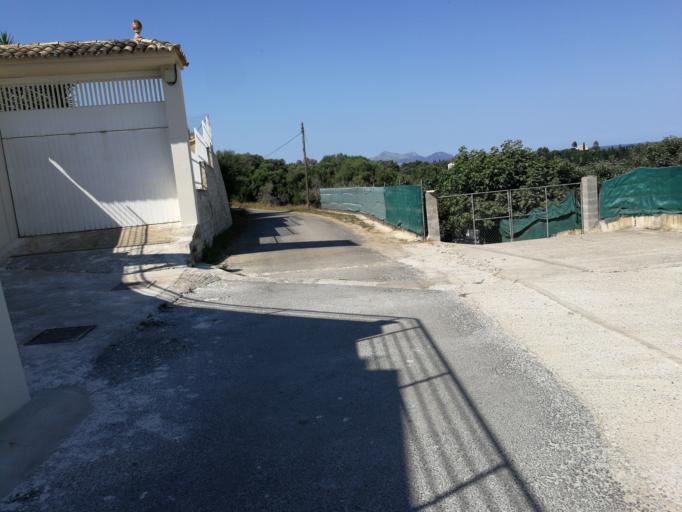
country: ES
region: Balearic Islands
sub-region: Illes Balears
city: Muro
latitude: 39.7360
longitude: 3.0744
